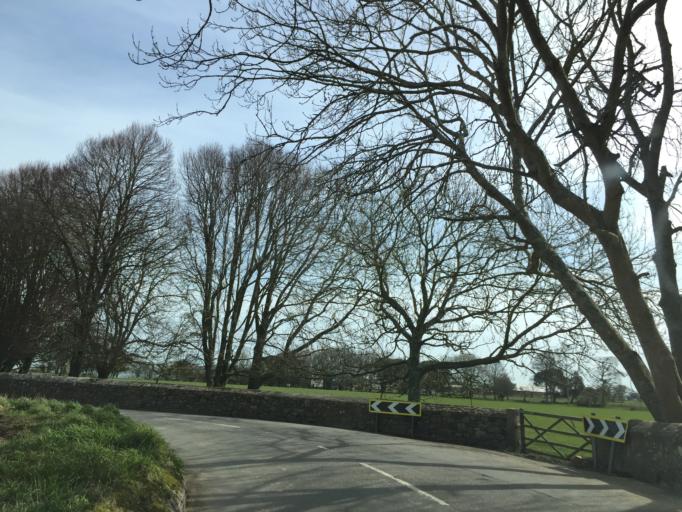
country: JE
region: St Helier
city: Saint Helier
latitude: 49.2282
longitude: -2.0444
